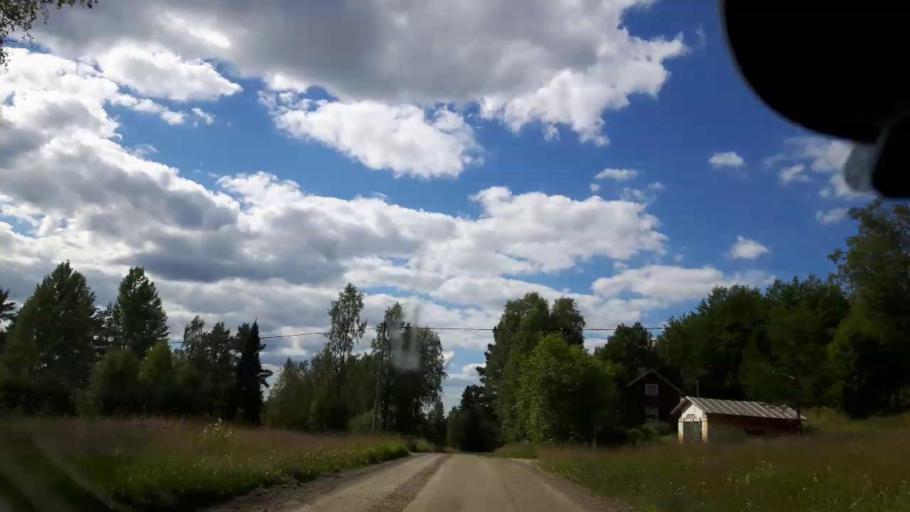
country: SE
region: Jaemtland
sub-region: Braecke Kommun
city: Braecke
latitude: 62.7244
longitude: 15.5377
